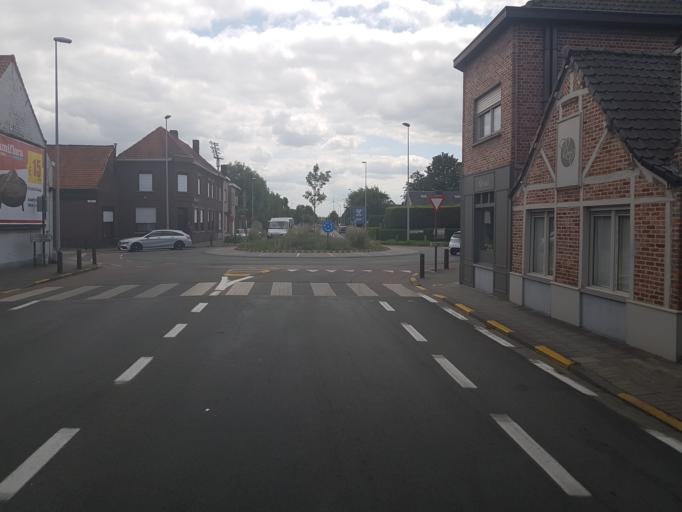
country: BE
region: Flanders
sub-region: Provincie West-Vlaanderen
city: Harelbeke
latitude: 50.8475
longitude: 3.3091
